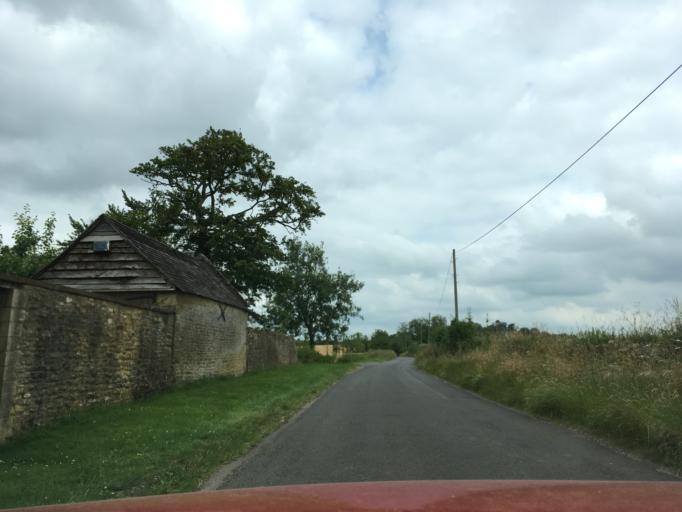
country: GB
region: England
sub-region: Oxfordshire
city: Charlbury
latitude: 51.9243
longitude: -1.4489
